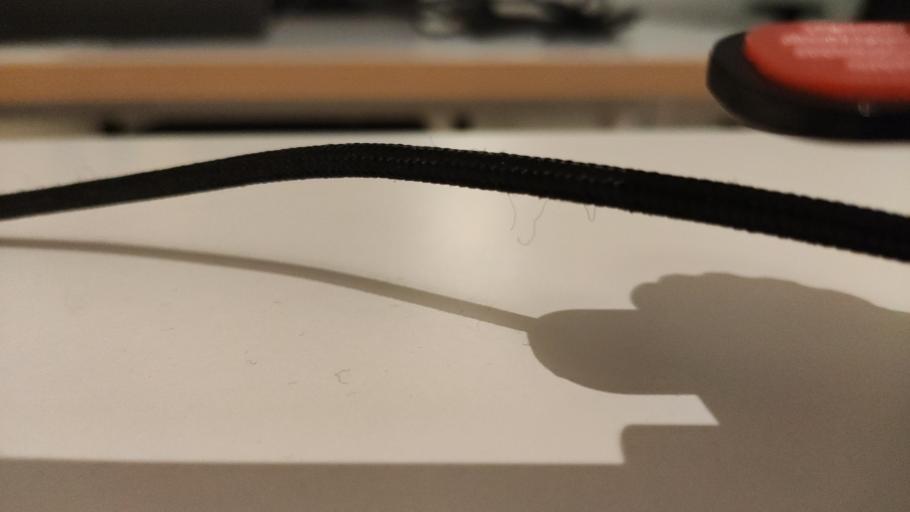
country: RU
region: Moskovskaya
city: Kurovskoye
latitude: 55.5703
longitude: 38.8840
